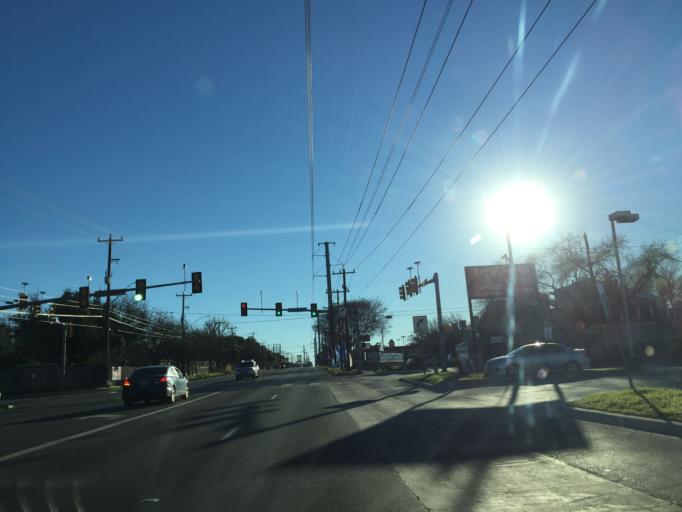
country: US
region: Texas
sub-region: Bexar County
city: Castle Hills
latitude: 29.5506
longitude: -98.5045
